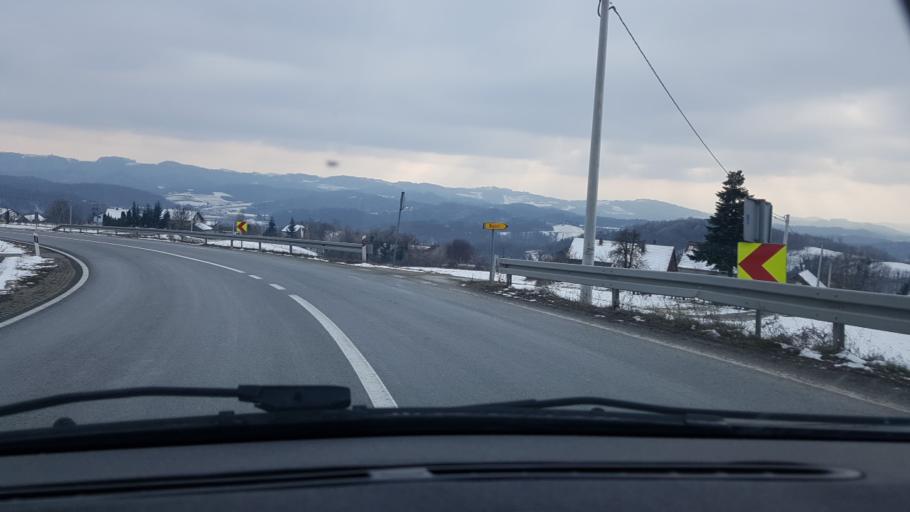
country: HR
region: Krapinsko-Zagorska
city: Mihovljan
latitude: 46.1614
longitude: 15.9607
